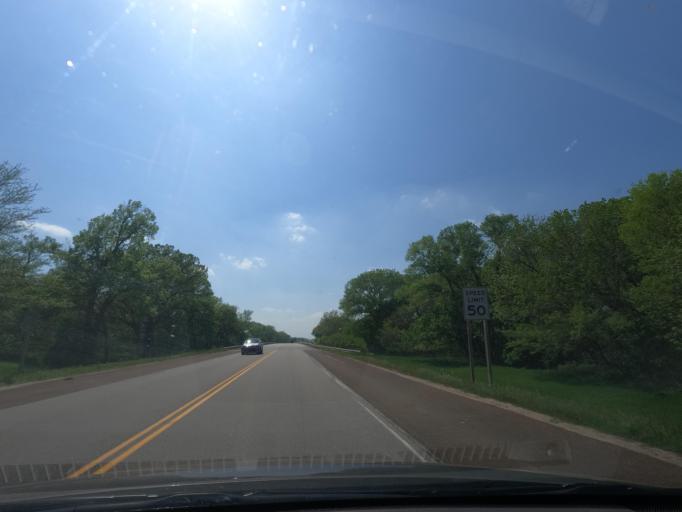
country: US
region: Kansas
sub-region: Butler County
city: Clay Center
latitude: 37.6797
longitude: -96.7769
